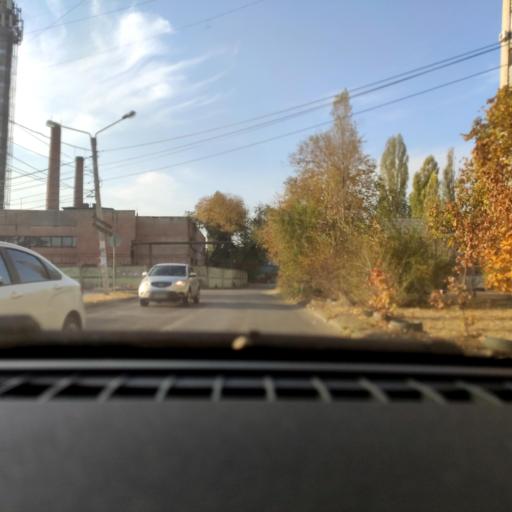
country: RU
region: Voronezj
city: Maslovka
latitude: 51.6358
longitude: 39.2727
